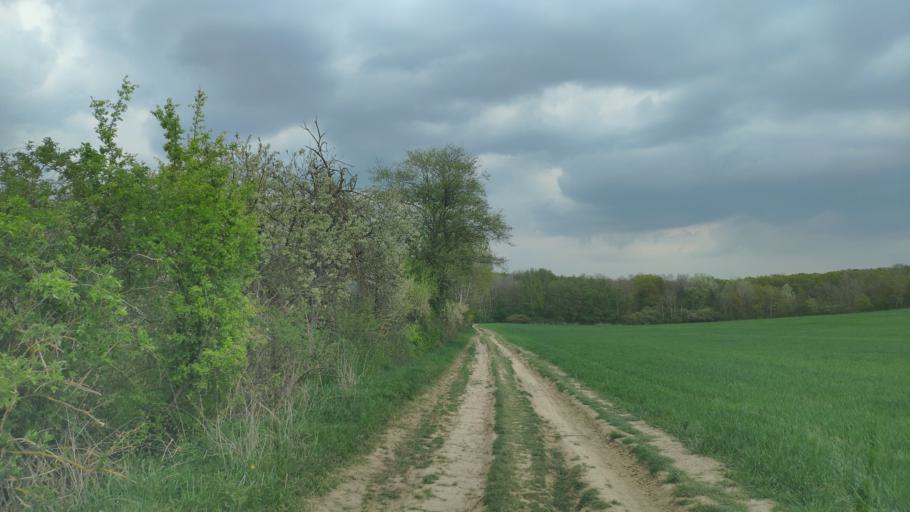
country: SK
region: Kosicky
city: Moldava nad Bodvou
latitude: 48.6158
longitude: 21.0394
